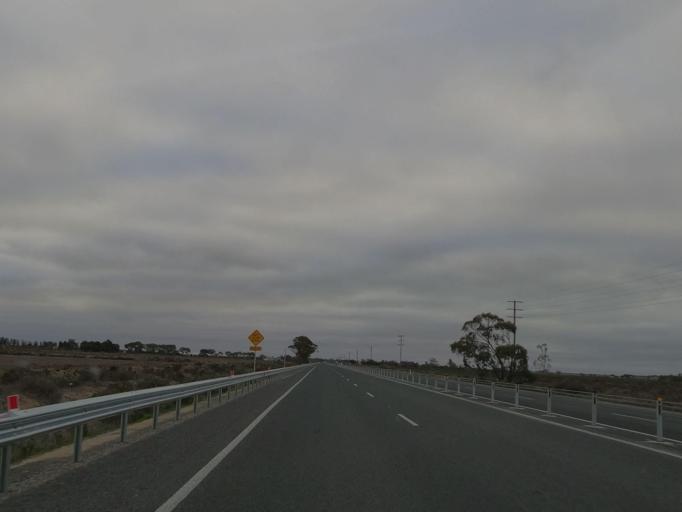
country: AU
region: Victoria
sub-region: Swan Hill
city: Swan Hill
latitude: -35.4786
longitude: 143.6872
